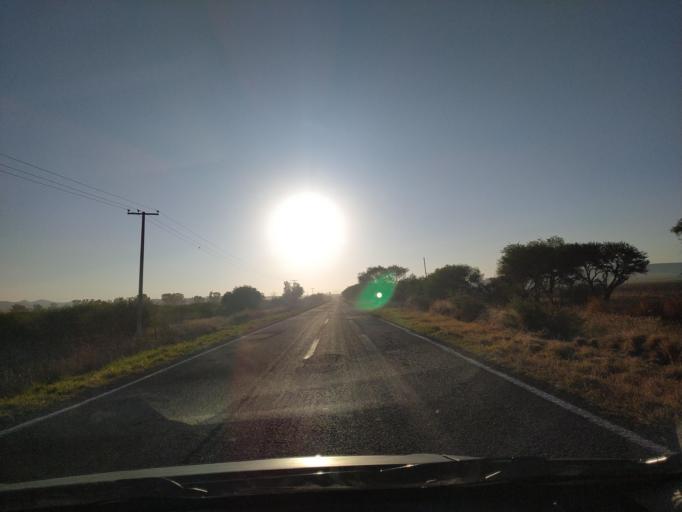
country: MX
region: Guanajuato
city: Ciudad Manuel Doblado
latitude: 20.7367
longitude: -101.8539
